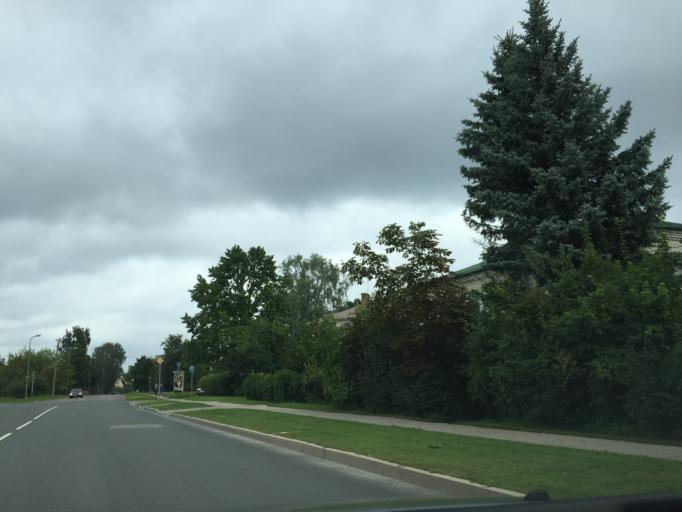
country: LV
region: Riga
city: Bergi
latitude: 56.9821
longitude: 24.2412
